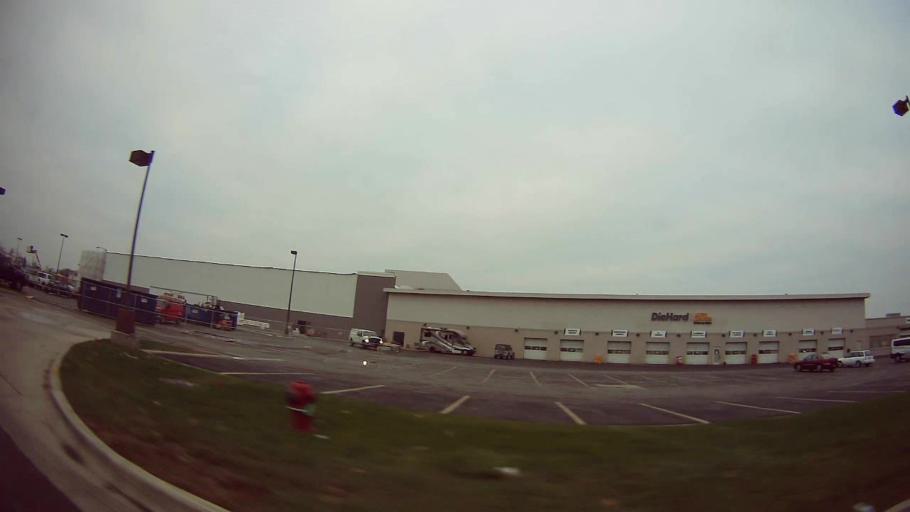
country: US
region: Michigan
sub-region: Oakland County
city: Clawson
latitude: 42.5372
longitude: -83.1073
